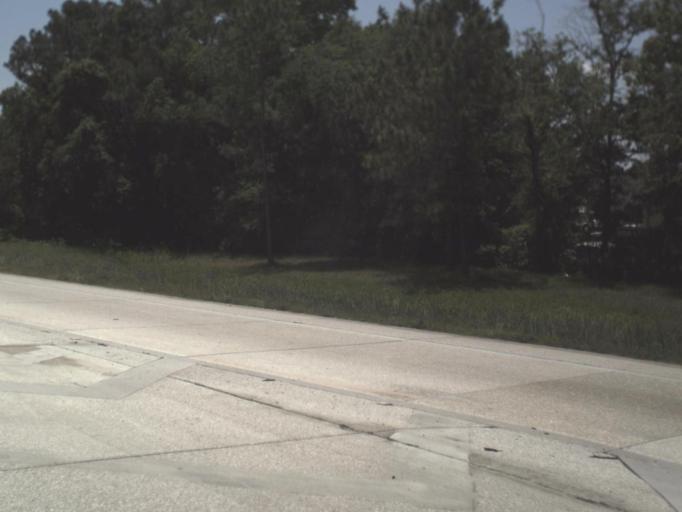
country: US
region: Florida
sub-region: Duval County
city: Jacksonville
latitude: 30.2628
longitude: -81.6076
